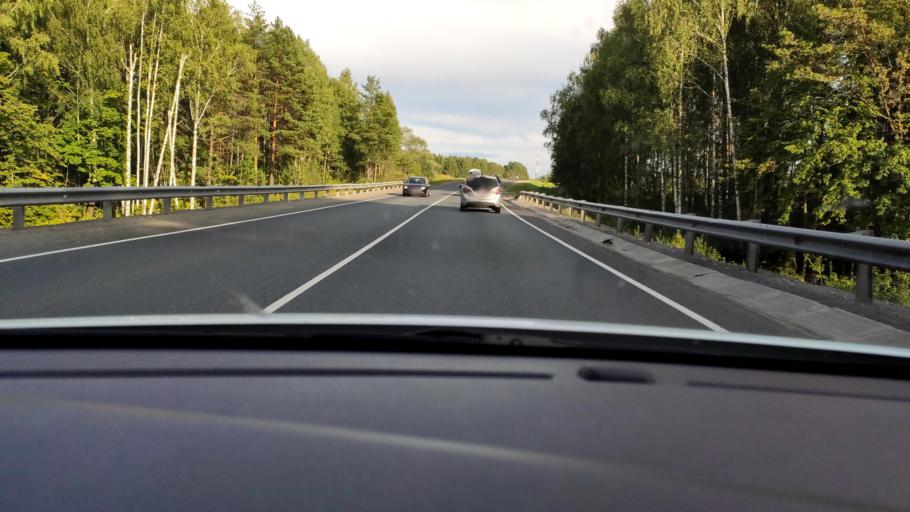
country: RU
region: Mariy-El
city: Krasnogorskiy
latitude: 56.1816
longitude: 48.2634
